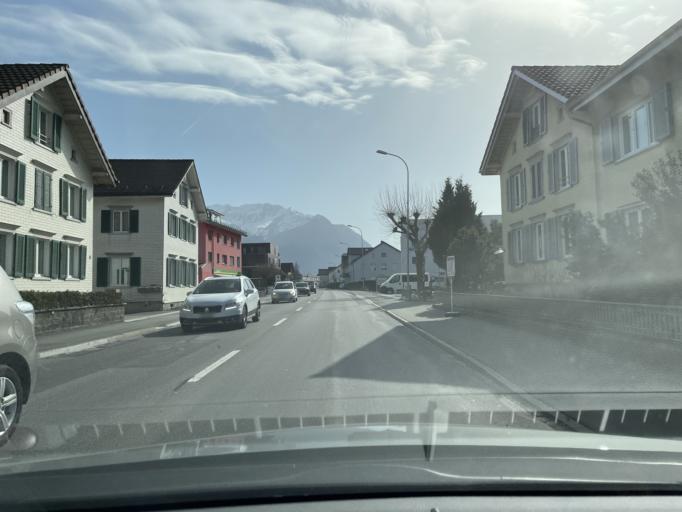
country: CH
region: Saint Gallen
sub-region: Wahlkreis Werdenberg
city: Buchs
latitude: 47.1512
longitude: 9.4819
